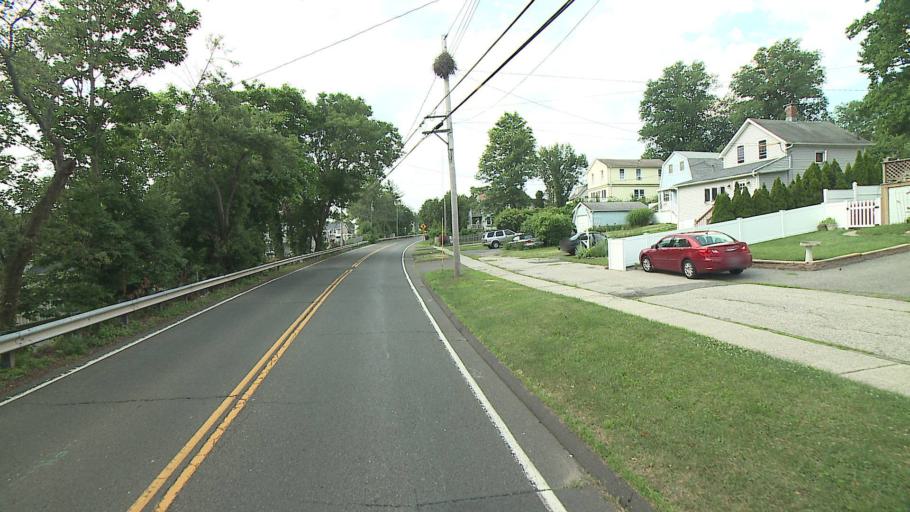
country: US
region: Connecticut
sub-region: New Haven County
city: Woodmont
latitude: 41.2174
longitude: -73.0071
